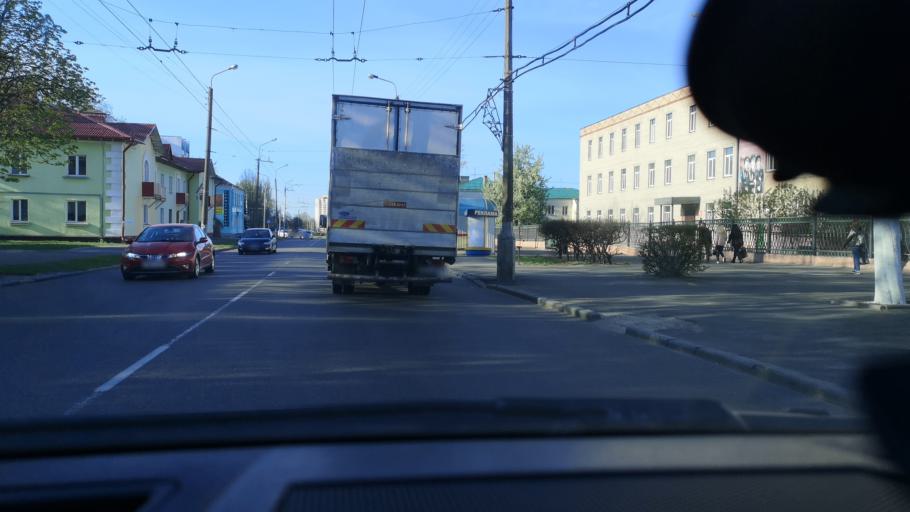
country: BY
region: Gomel
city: Gomel
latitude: 52.4205
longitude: 30.9727
